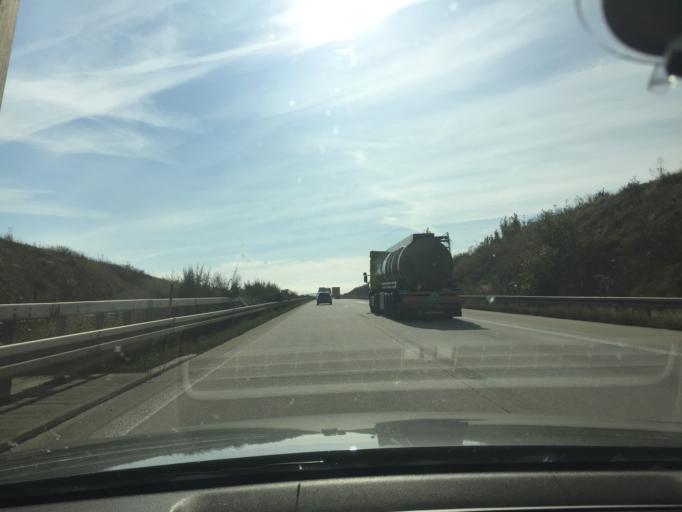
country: DE
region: Saxony
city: Dohma
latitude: 50.9167
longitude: 13.8919
